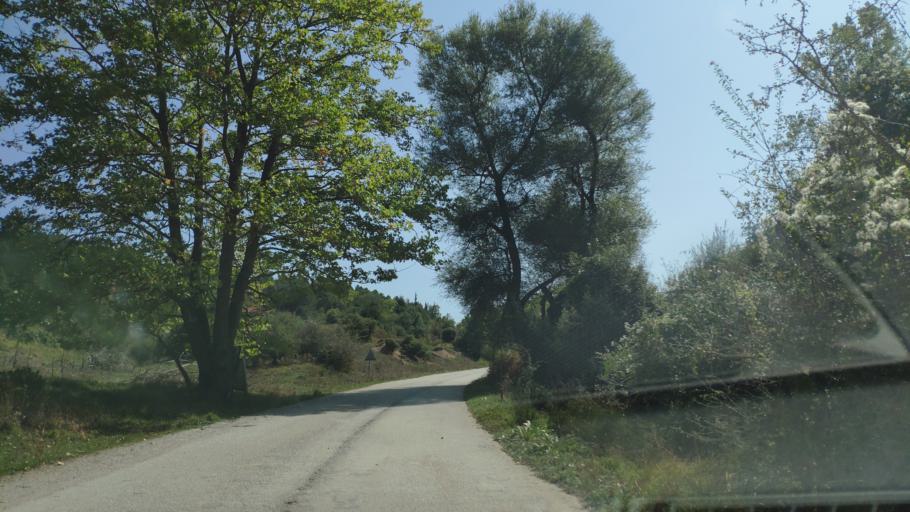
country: GR
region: West Greece
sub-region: Nomos Achaias
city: Kalavryta
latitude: 37.9231
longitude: 22.2938
